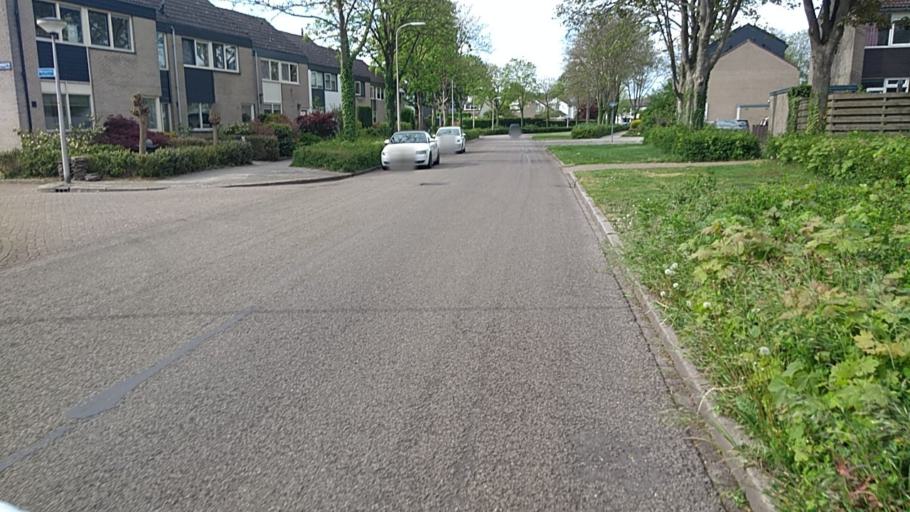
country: NL
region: Overijssel
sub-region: Gemeente Almelo
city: Almelo
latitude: 52.3768
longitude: 6.6708
